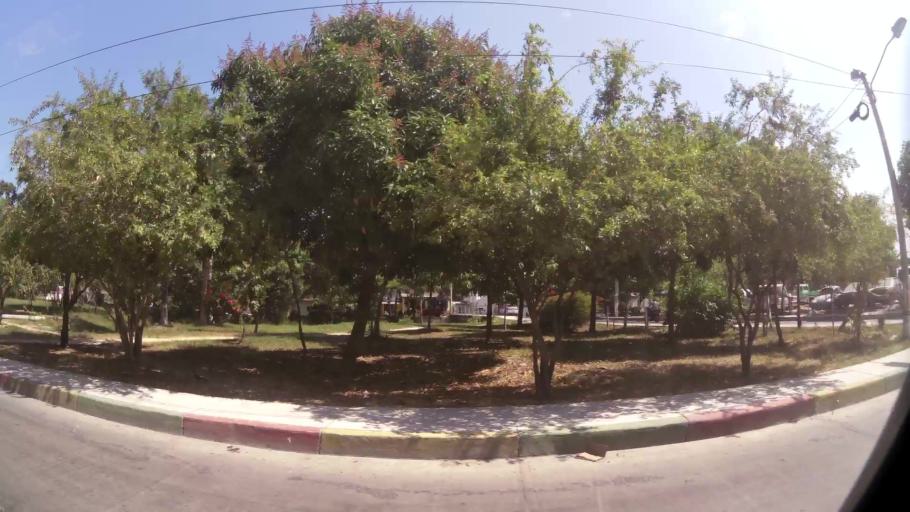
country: CO
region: Bolivar
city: Cartagena
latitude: 10.3990
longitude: -75.4862
